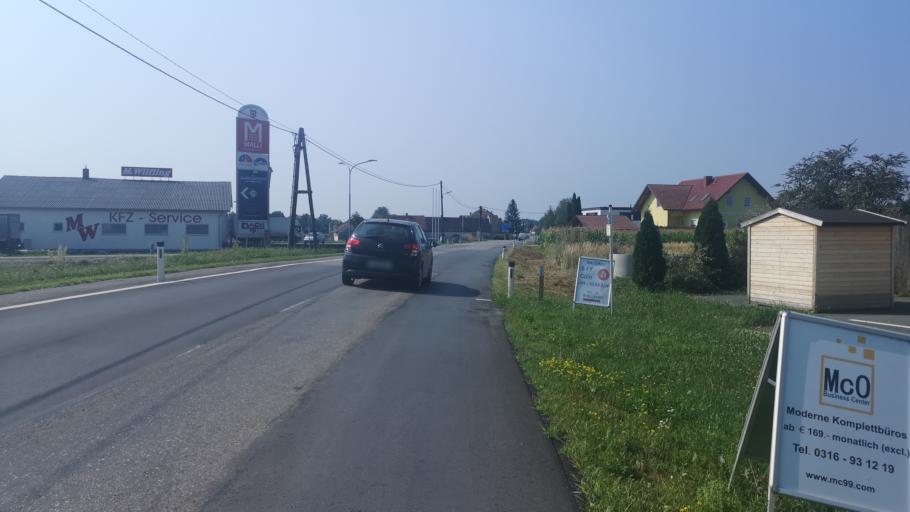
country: AT
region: Styria
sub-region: Politischer Bezirk Graz-Umgebung
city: Seiersberg
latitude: 46.9967
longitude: 15.4004
